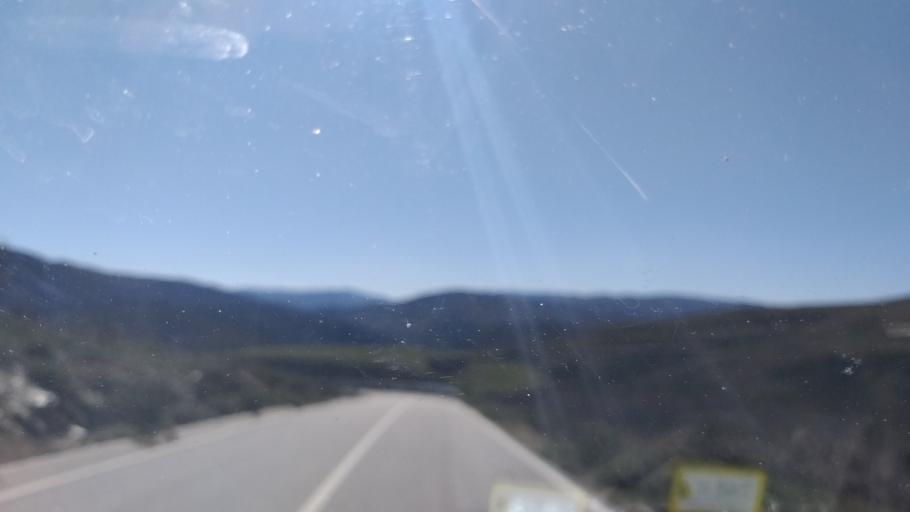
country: PT
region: Guarda
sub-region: Manteigas
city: Manteigas
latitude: 40.4642
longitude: -7.5030
